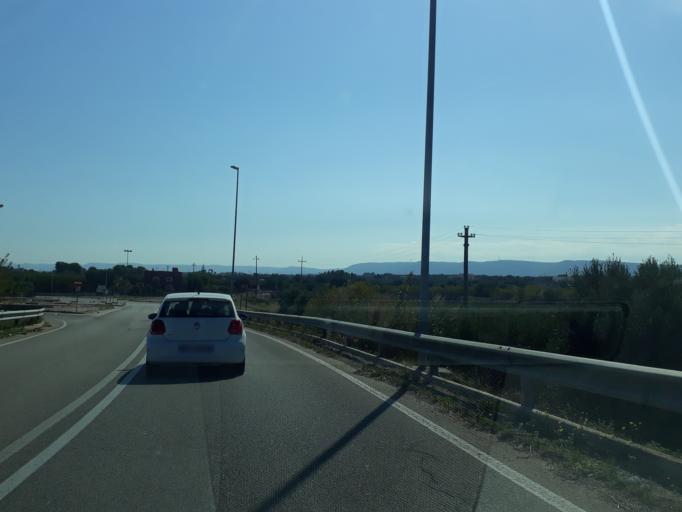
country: IT
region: Apulia
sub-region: Provincia di Bari
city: Monopoli
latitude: 40.9206
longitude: 17.3153
